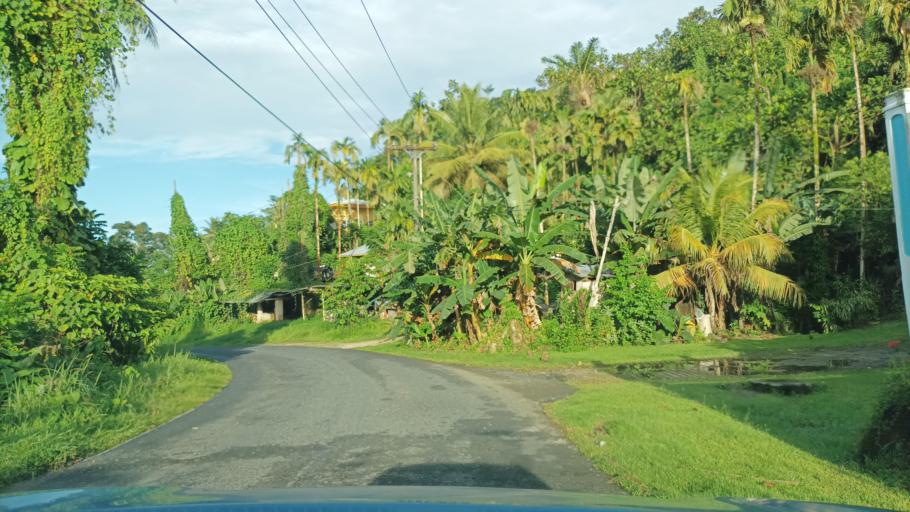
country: FM
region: Pohnpei
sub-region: Kolonia Municipality
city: Kolonia Town
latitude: 6.9554
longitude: 158.1979
